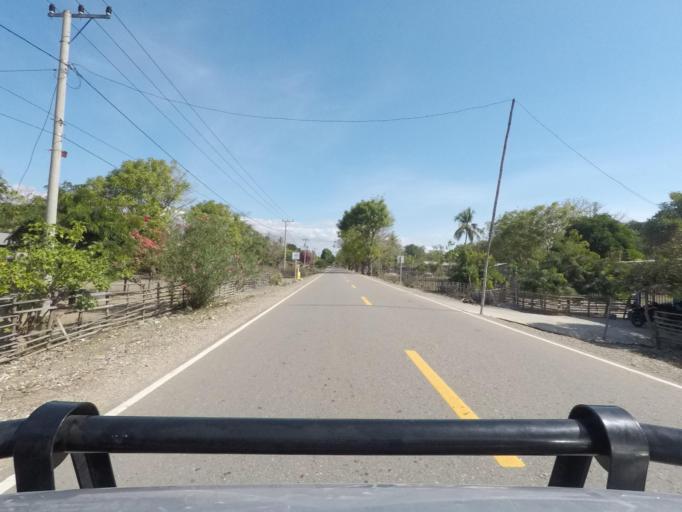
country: ID
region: East Nusa Tenggara
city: Atambua
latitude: -8.8967
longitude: 125.0021
